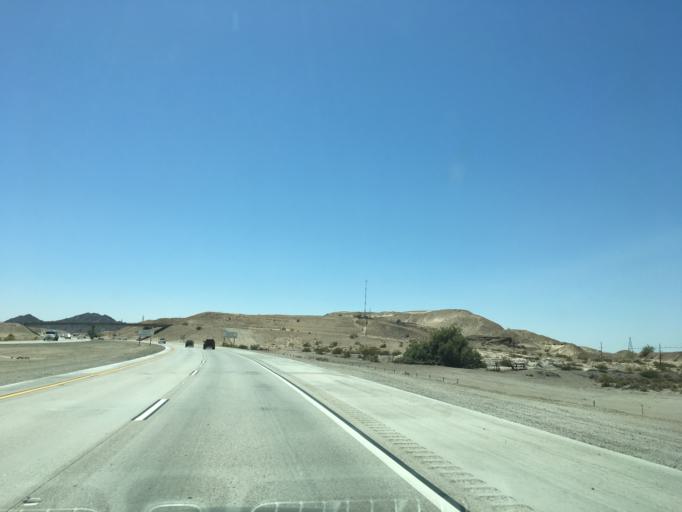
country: MX
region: Baja California
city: Los Algodones
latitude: 32.7474
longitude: -114.7001
